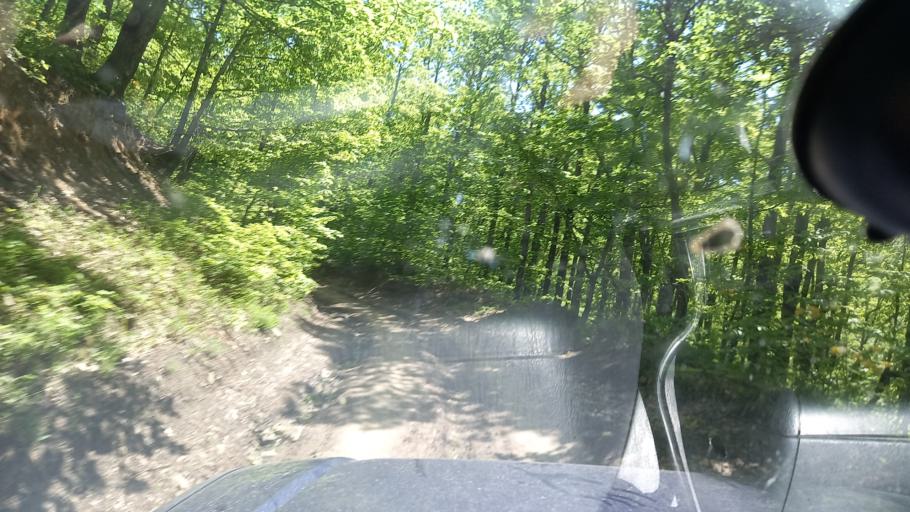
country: RU
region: Krasnodarskiy
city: Tuapse
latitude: 44.2623
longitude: 39.2791
